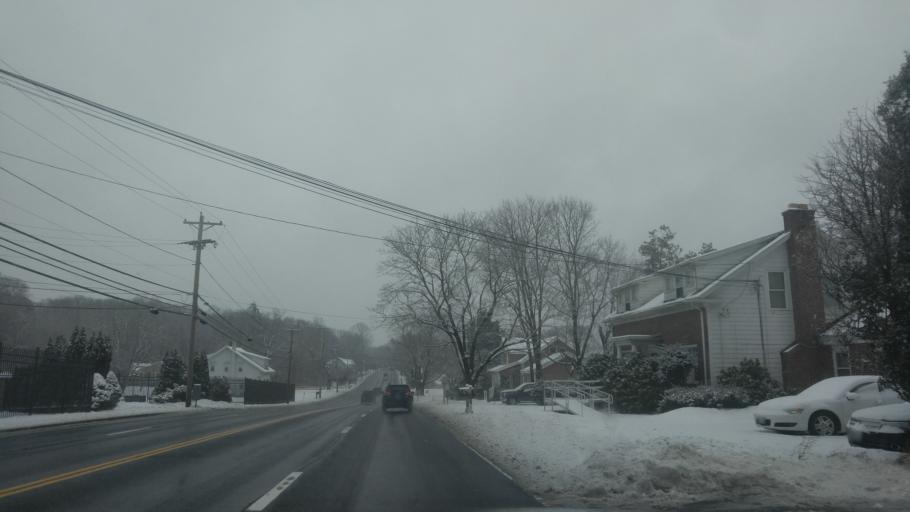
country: US
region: Rhode Island
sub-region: Providence County
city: Johnston
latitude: 41.8312
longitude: -71.5437
